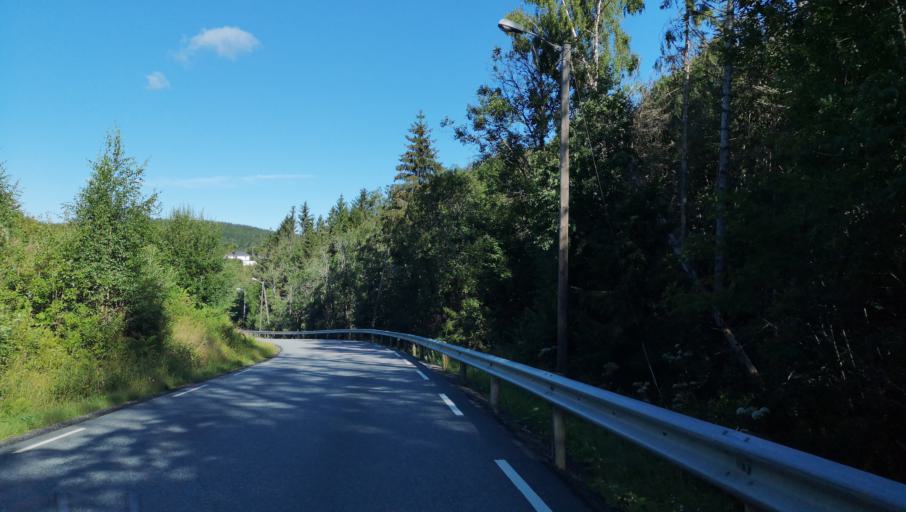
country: NO
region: Ostfold
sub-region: Hobol
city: Tomter
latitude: 59.6553
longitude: 11.0079
